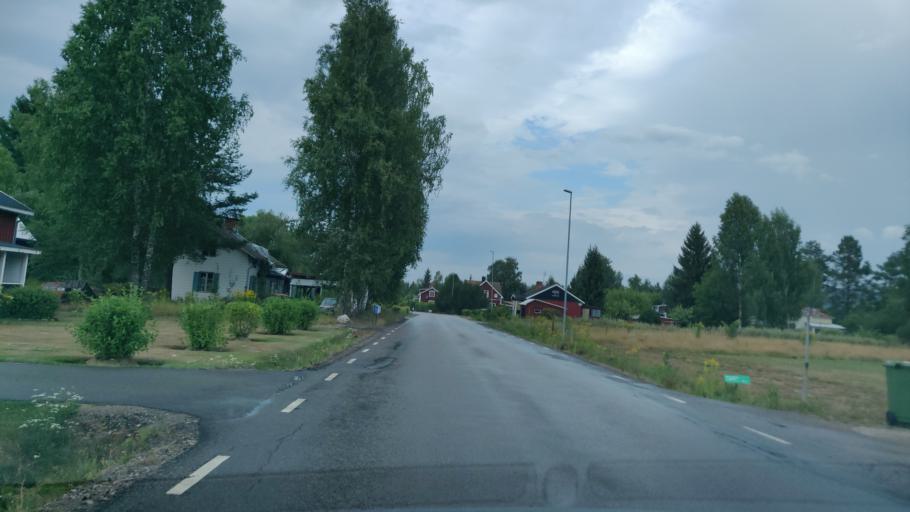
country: SE
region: Vaermland
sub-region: Munkfors Kommun
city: Munkfors
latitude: 59.8535
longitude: 13.5540
